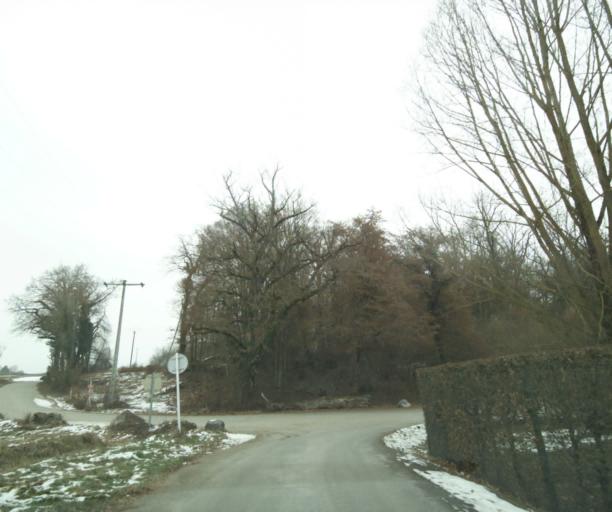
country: FR
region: Rhone-Alpes
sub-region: Departement de la Haute-Savoie
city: Reignier-Esery
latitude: 46.1363
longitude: 6.2964
